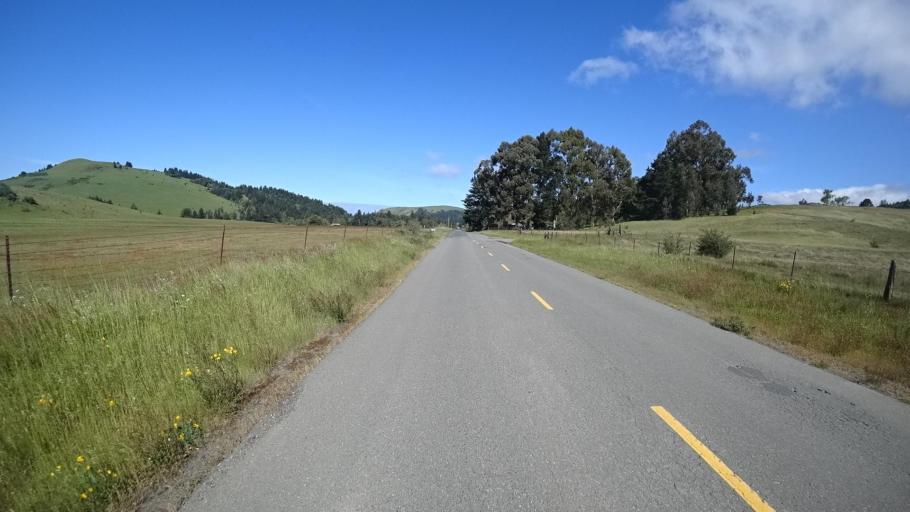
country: US
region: California
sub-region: Humboldt County
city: Ferndale
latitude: 40.3380
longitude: -124.3117
